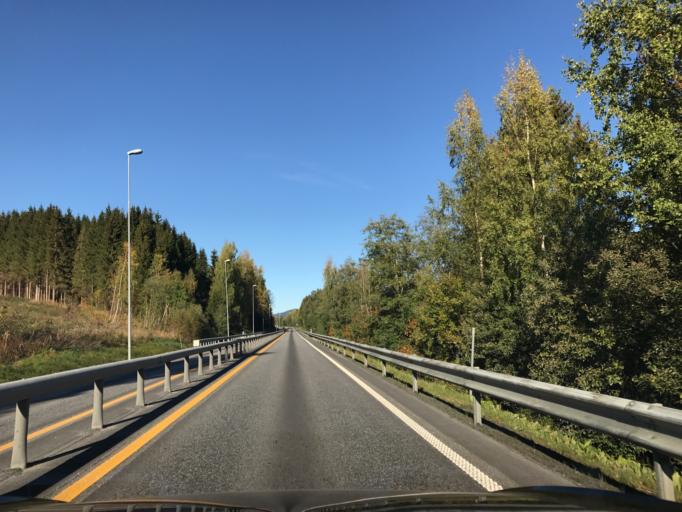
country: NO
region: Oppland
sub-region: Lillehammer
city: Lillehammer
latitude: 61.0070
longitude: 10.4848
